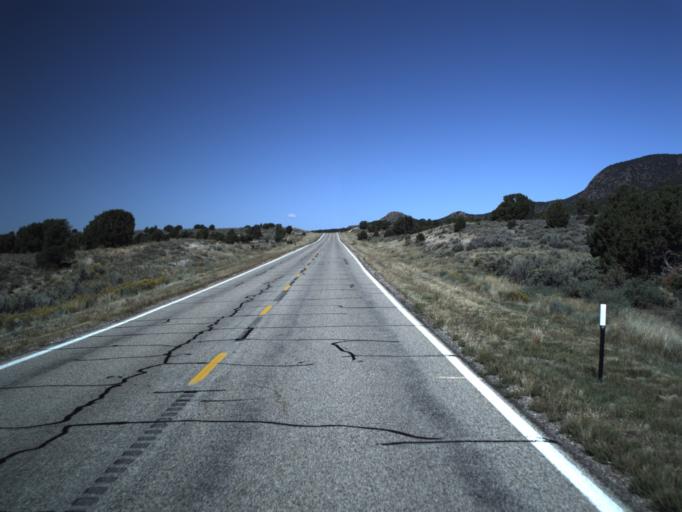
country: US
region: Utah
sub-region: Washington County
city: Enterprise
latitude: 37.6487
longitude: -113.4473
